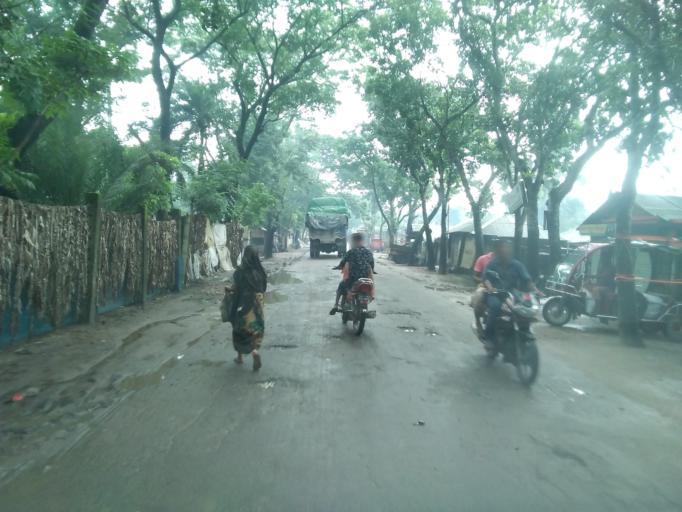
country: IN
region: West Bengal
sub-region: North 24 Parganas
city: Taki
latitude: 22.3491
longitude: 89.1034
